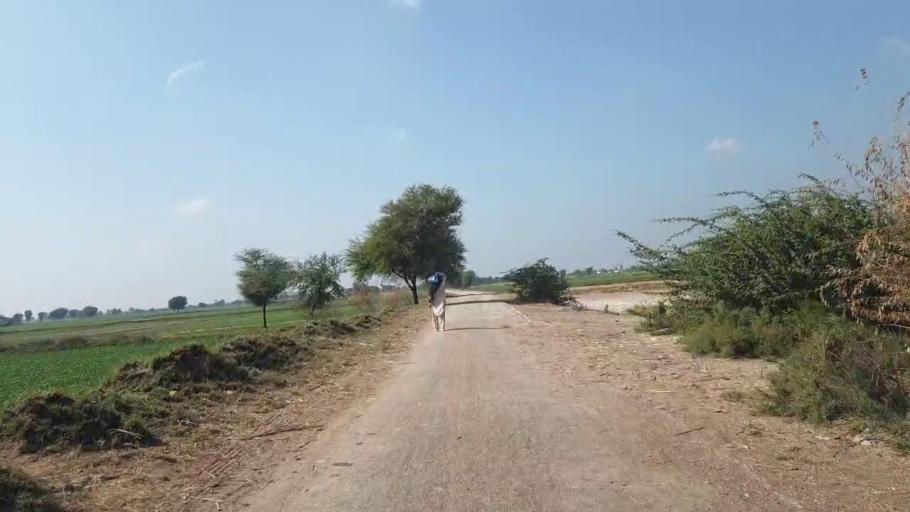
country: PK
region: Sindh
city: Shahdadpur
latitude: 26.0411
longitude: 68.5895
